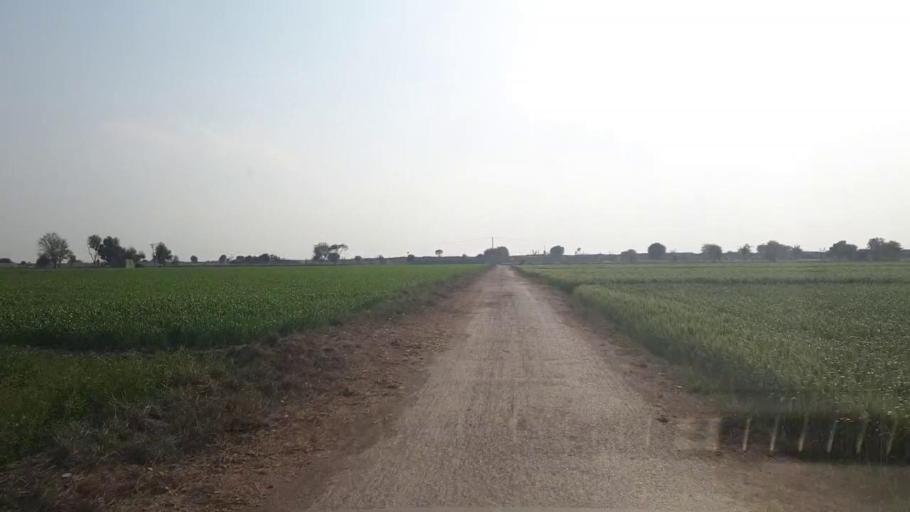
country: PK
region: Sindh
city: Hala
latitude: 25.8463
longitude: 68.3904
